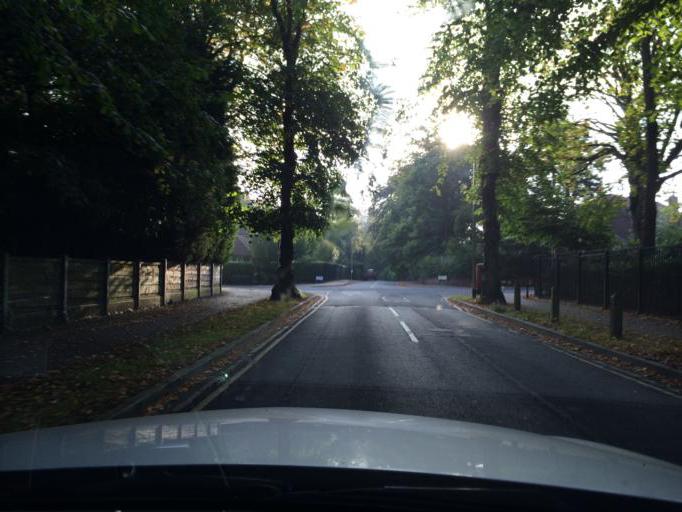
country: GB
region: England
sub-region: Borough of Stockport
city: Bramhall
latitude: 53.3731
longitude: -2.1728
